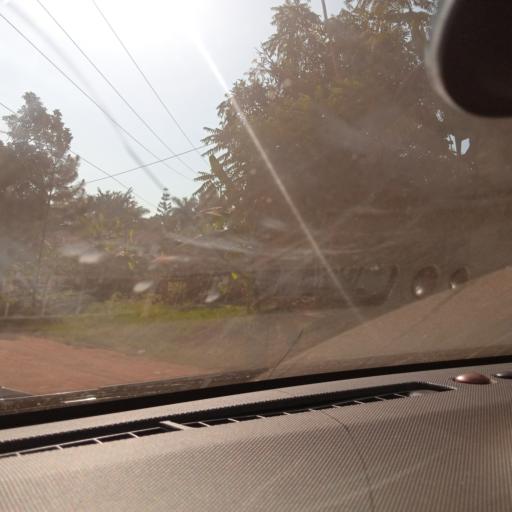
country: UG
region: Central Region
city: Masaka
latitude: -0.3337
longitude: 31.7347
